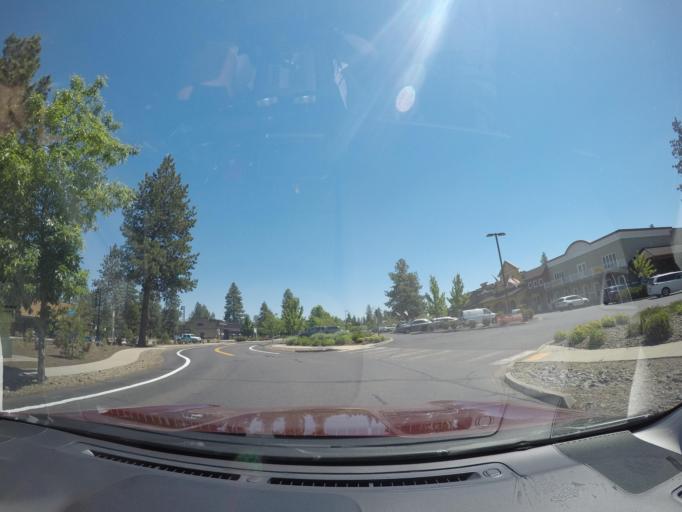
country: US
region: Oregon
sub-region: Deschutes County
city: Sisters
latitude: 44.2974
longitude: -121.5624
